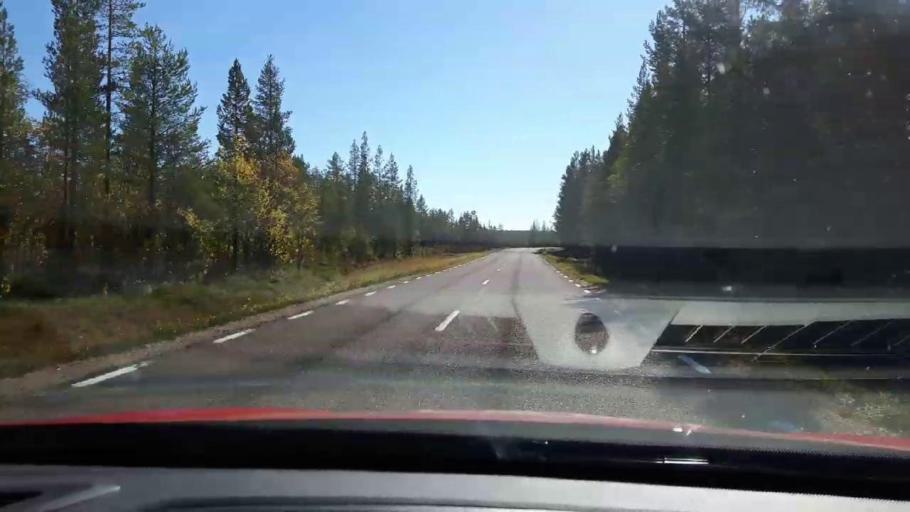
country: SE
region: Jaemtland
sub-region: Harjedalens Kommun
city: Sveg
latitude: 61.7421
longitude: 14.1606
